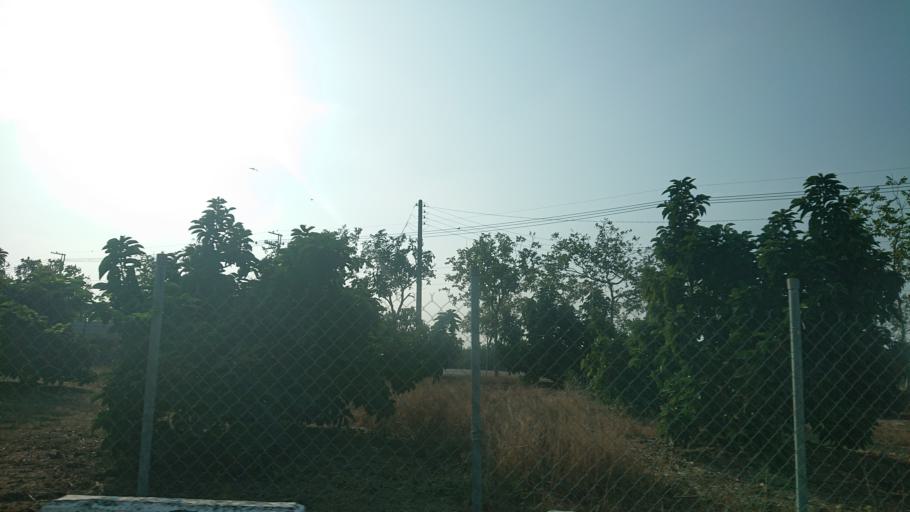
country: TW
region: Taiwan
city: Xinying
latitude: 23.2037
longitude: 120.2710
